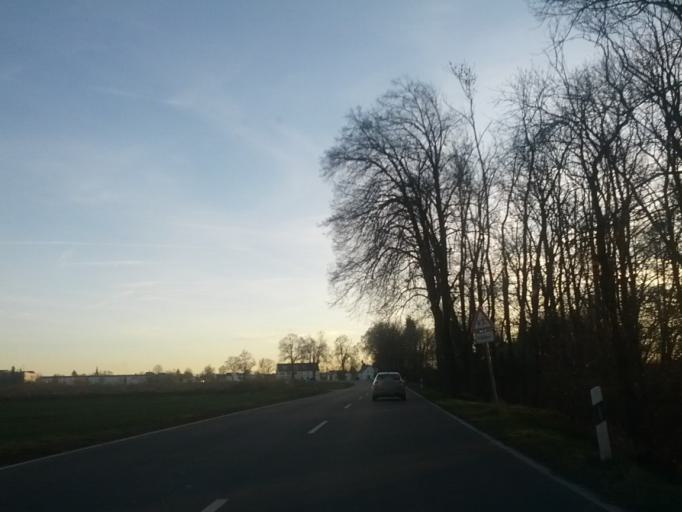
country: DE
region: Bavaria
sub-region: Swabia
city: Fellheim
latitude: 48.0834
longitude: 10.1509
